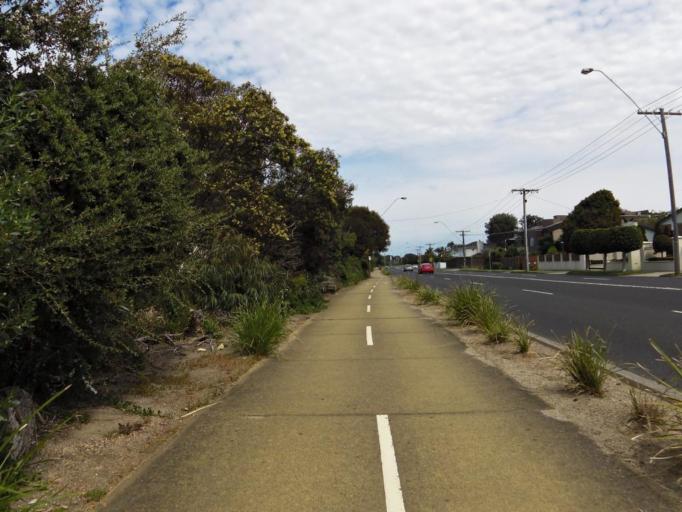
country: AU
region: Victoria
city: Beaumaris
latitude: -37.9935
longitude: 145.0406
